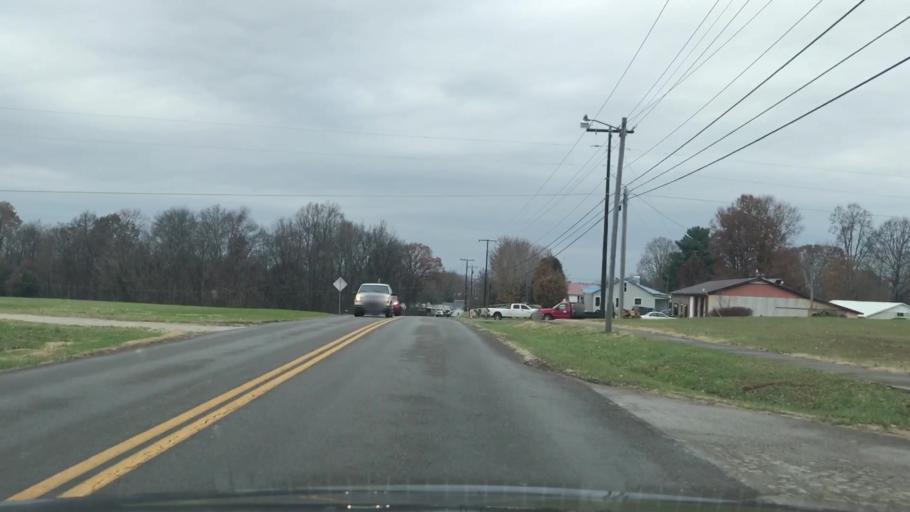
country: US
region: Kentucky
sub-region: Metcalfe County
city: Edmonton
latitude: 36.9729
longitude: -85.6096
